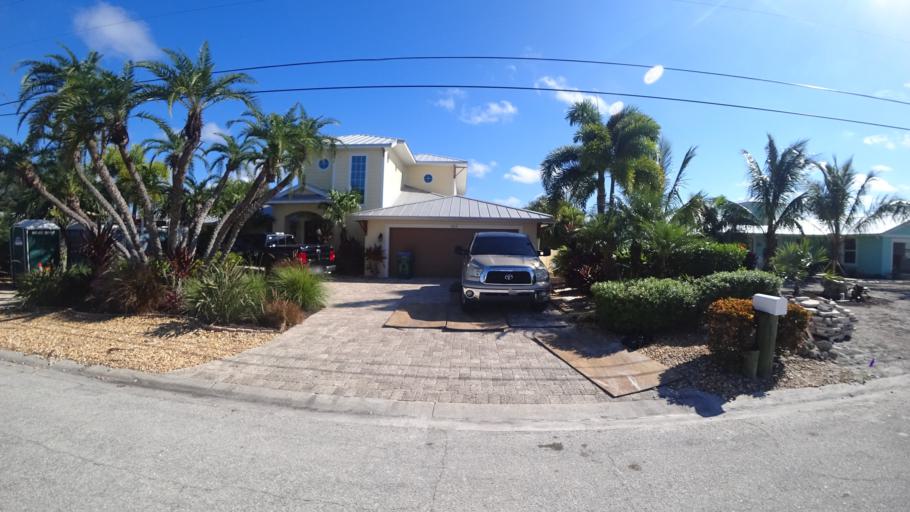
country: US
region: Florida
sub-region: Manatee County
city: Anna Maria
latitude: 27.5177
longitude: -82.7164
